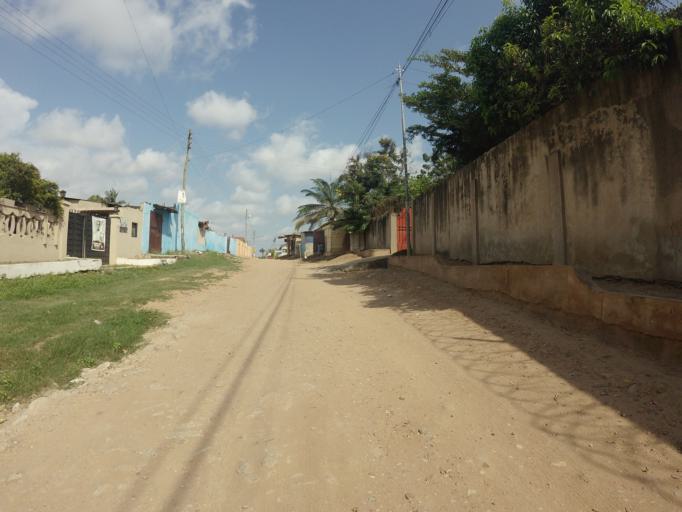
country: GH
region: Greater Accra
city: Dome
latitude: 5.6174
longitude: -0.2405
